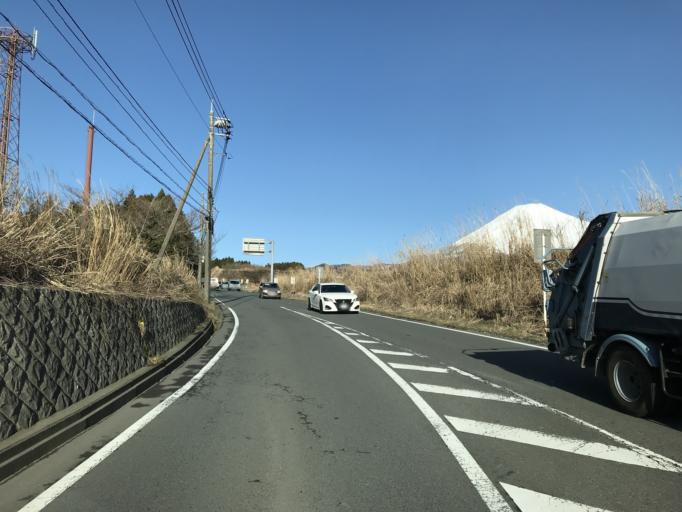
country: JP
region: Shizuoka
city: Gotemba
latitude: 35.2616
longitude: 138.8620
